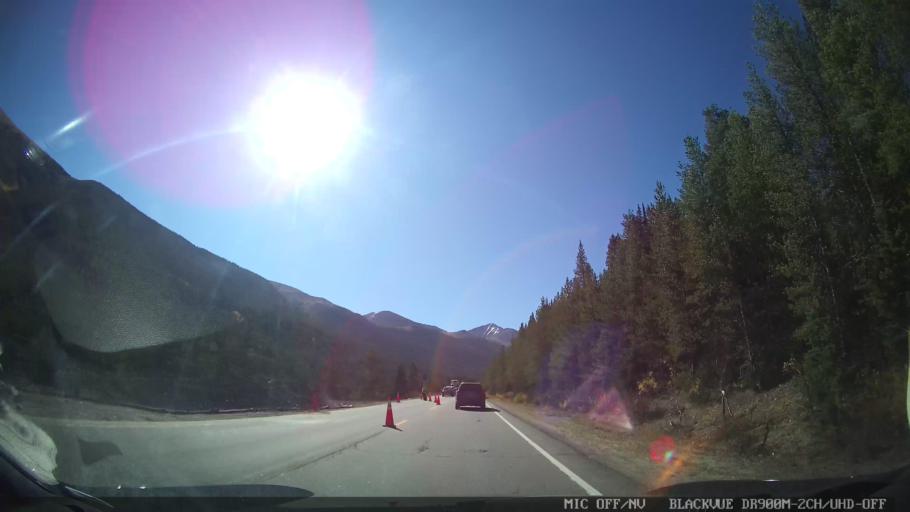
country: US
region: Colorado
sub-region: Summit County
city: Frisco
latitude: 39.4920
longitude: -106.1357
